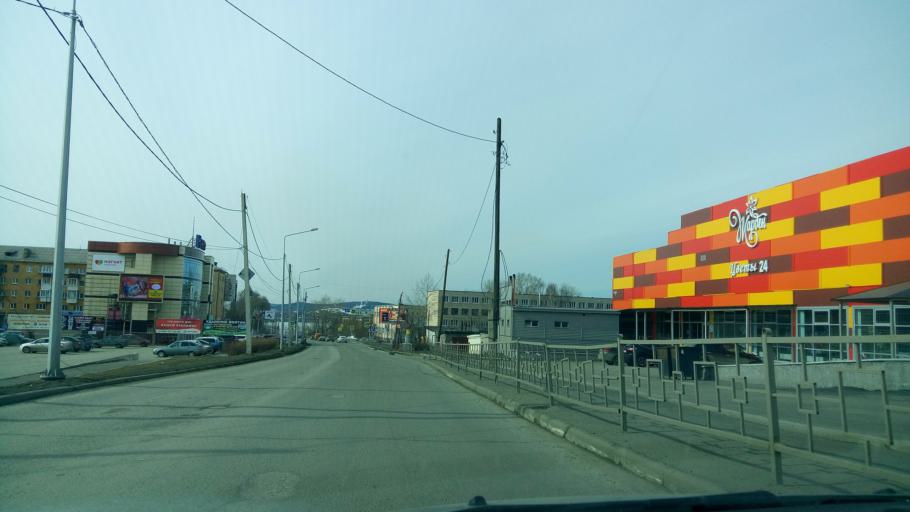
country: RU
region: Sverdlovsk
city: Nizhniy Tagil
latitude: 57.9058
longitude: 59.9976
